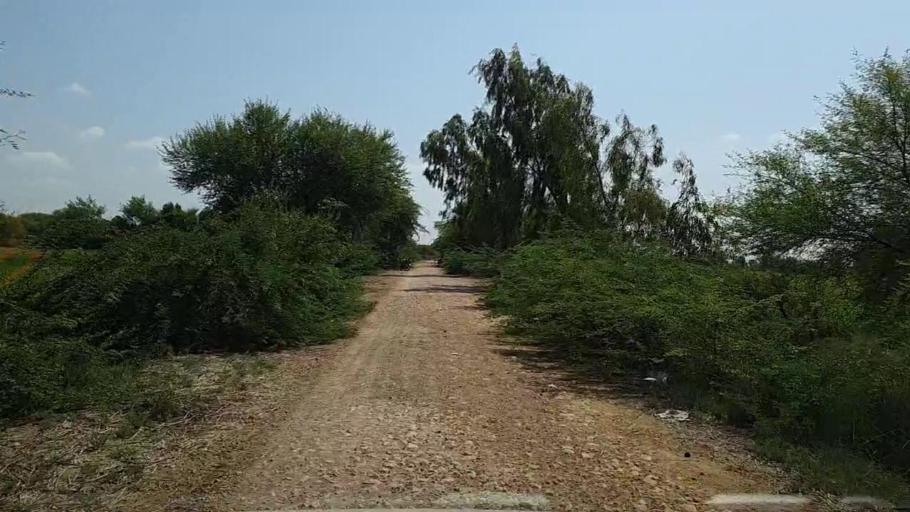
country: PK
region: Sindh
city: Kario
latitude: 24.7027
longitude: 68.6157
